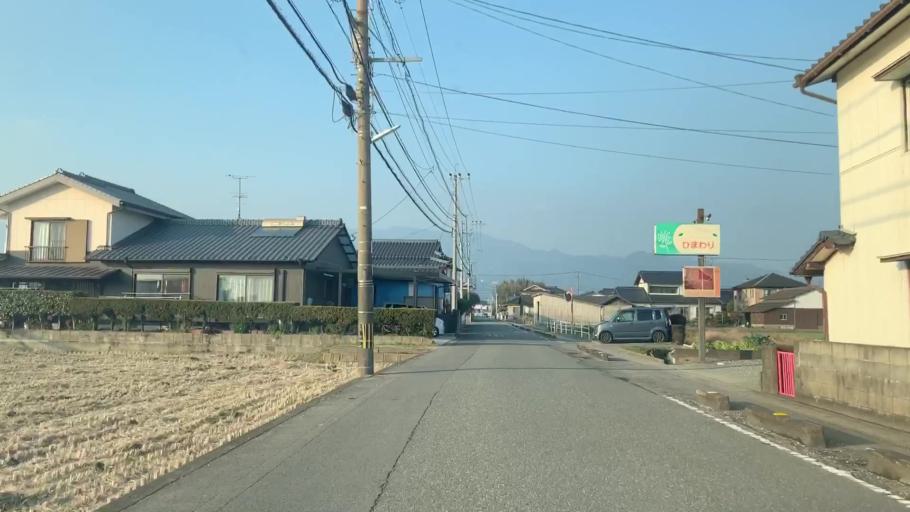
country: JP
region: Saga Prefecture
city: Saga-shi
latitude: 33.2778
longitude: 130.2264
